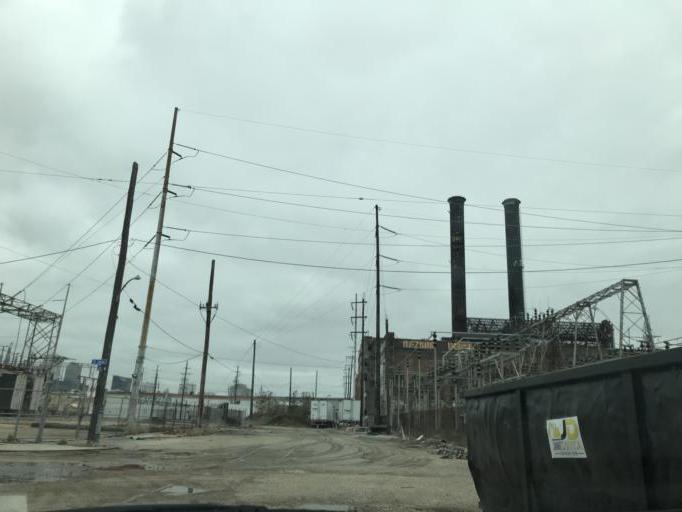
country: US
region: Louisiana
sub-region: Jefferson Parish
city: Gretna
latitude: 29.9285
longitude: -90.0654
